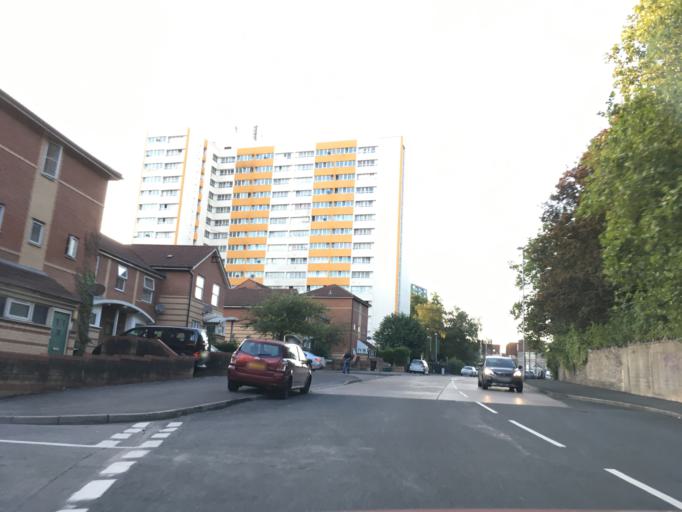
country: GB
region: England
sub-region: Bristol
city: Bristol
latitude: 51.4531
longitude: -2.5598
